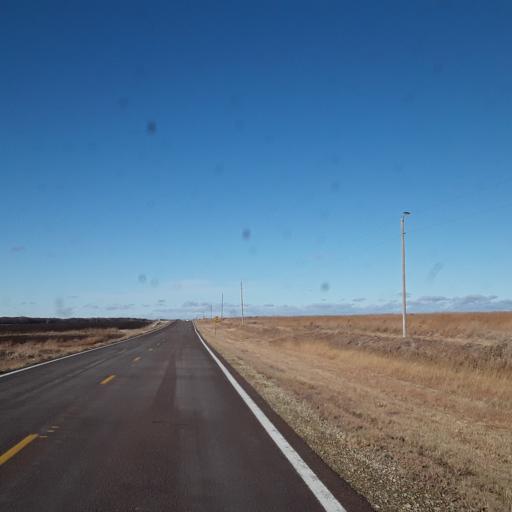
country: US
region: Kansas
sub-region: Cloud County
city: Concordia
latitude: 39.5207
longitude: -97.7228
